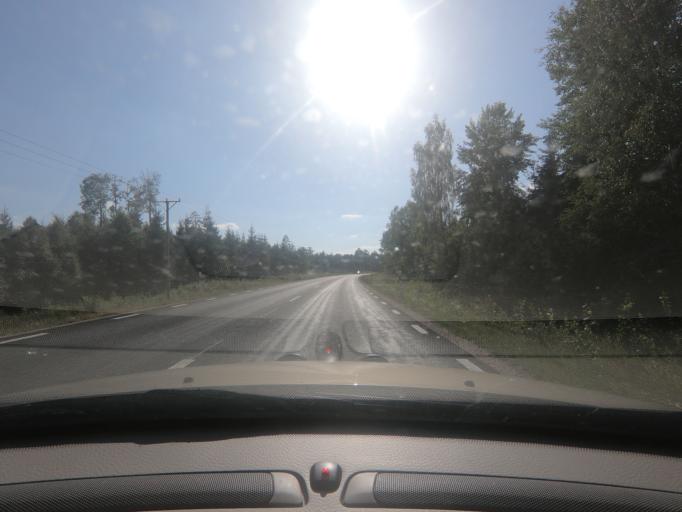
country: SE
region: Joenkoeping
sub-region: Vetlanda Kommun
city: Vetlanda
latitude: 57.4171
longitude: 15.0328
